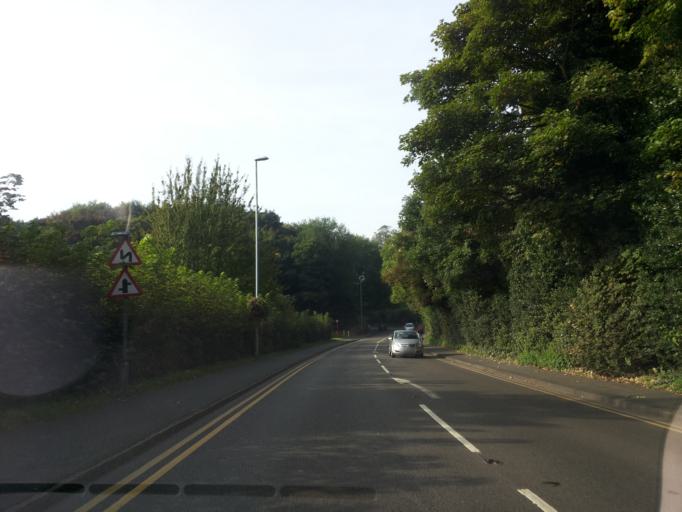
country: GB
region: England
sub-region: Worcestershire
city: Stourport-on-Severn
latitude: 52.3358
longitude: -2.2846
